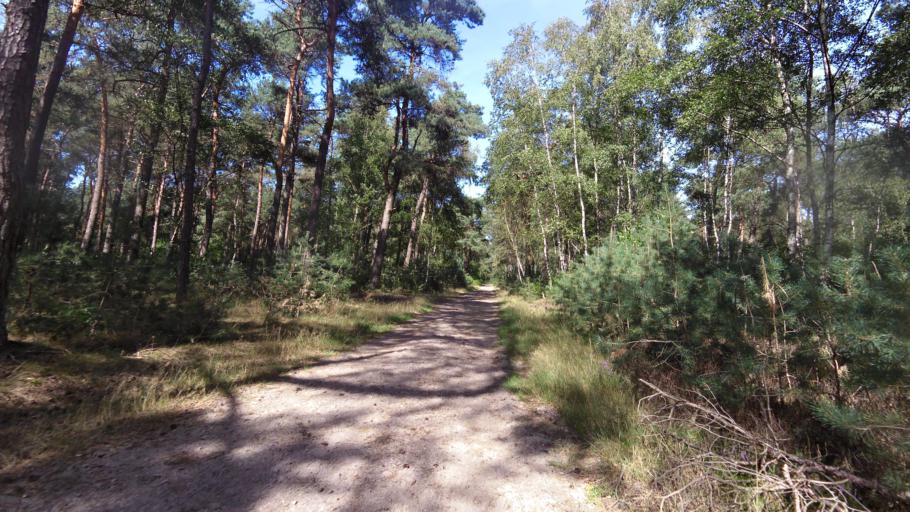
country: NL
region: Gelderland
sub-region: Gemeente Ede
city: Otterlo
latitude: 52.0457
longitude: 5.7464
